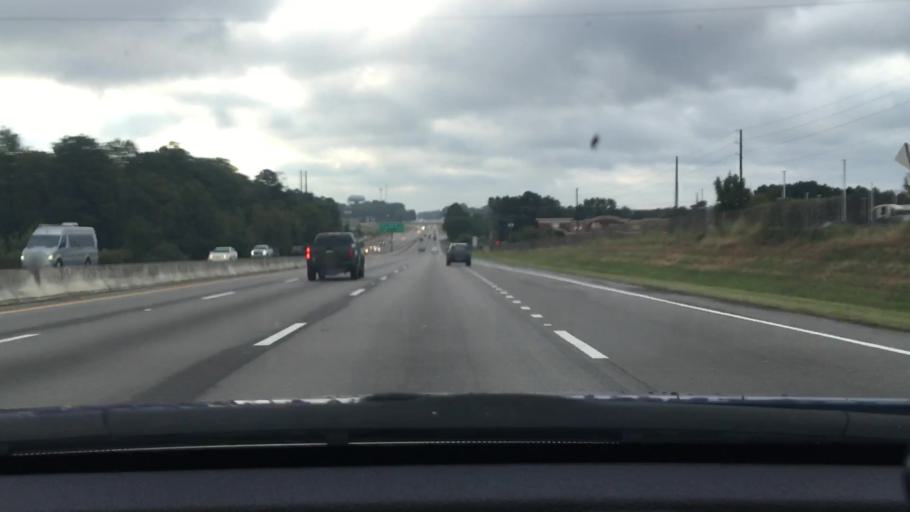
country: US
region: South Carolina
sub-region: Lexington County
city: Seven Oaks
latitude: 34.0748
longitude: -81.1497
